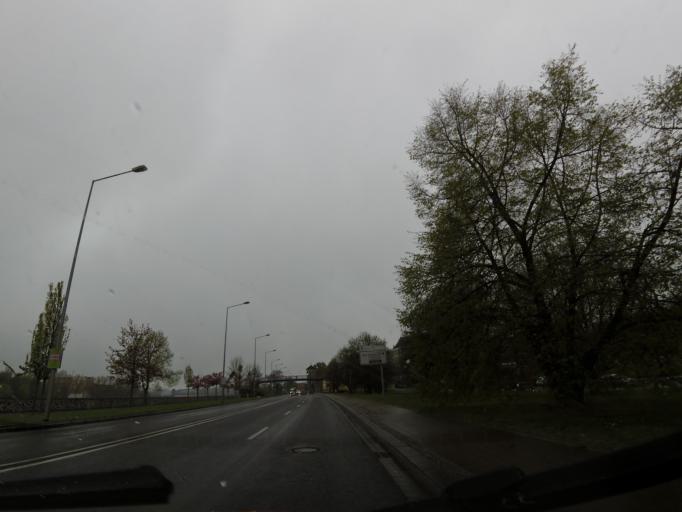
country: DE
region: Saxony-Anhalt
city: Magdeburg
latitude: 52.1269
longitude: 11.6394
